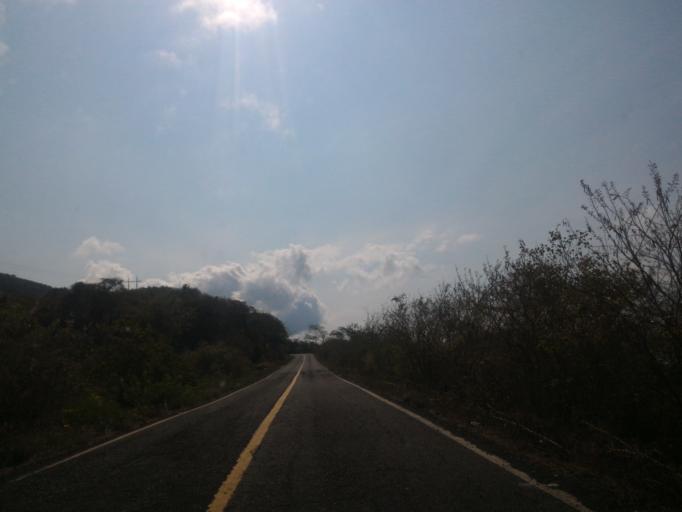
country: MX
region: Michoacan
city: Coahuayana Viejo
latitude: 18.4798
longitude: -103.5649
